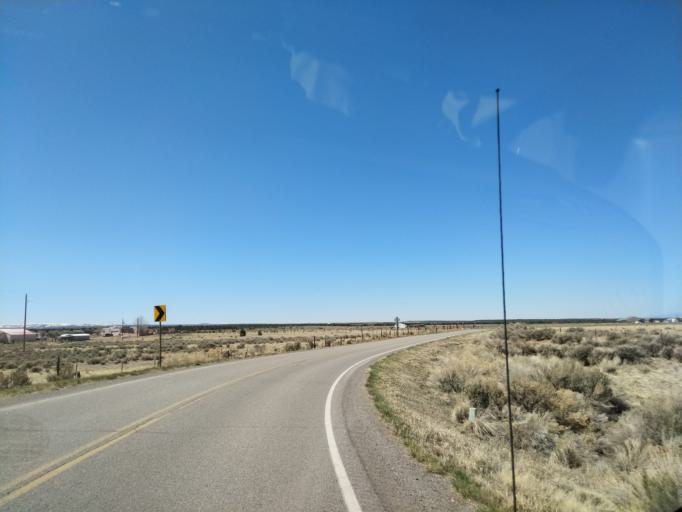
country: US
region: Colorado
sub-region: Mesa County
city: Redlands
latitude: 38.9906
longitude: -108.7518
